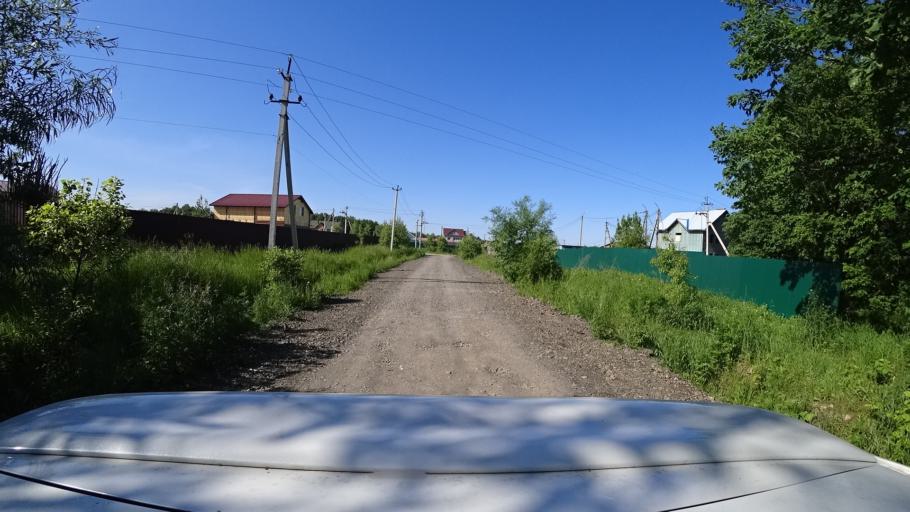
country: RU
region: Khabarovsk Krai
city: Topolevo
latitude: 48.5486
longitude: 135.1827
